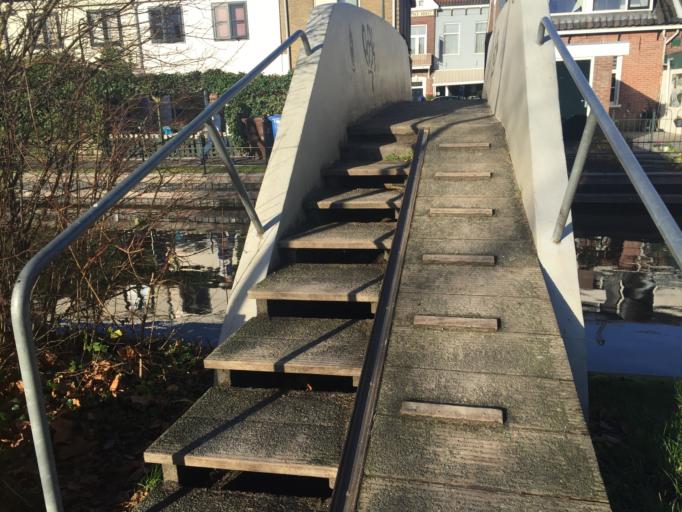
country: NL
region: Utrecht
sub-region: Gemeente Montfoort
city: Montfoort
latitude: 52.0901
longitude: 4.9578
